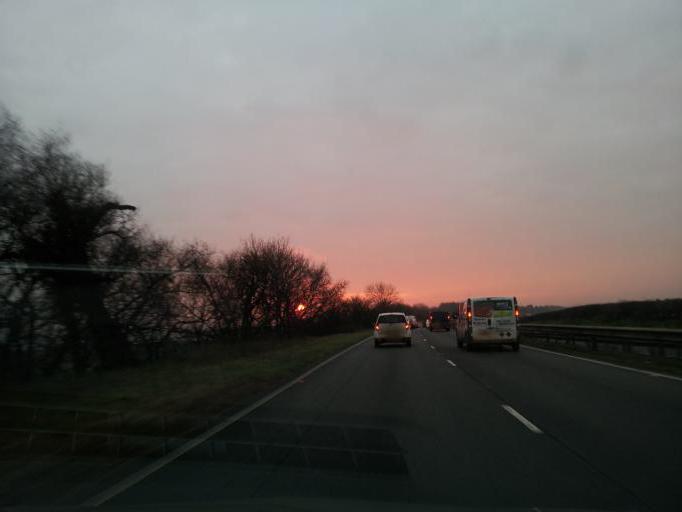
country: GB
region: England
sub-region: Peterborough
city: Thornhaugh
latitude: 52.6027
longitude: -0.4253
